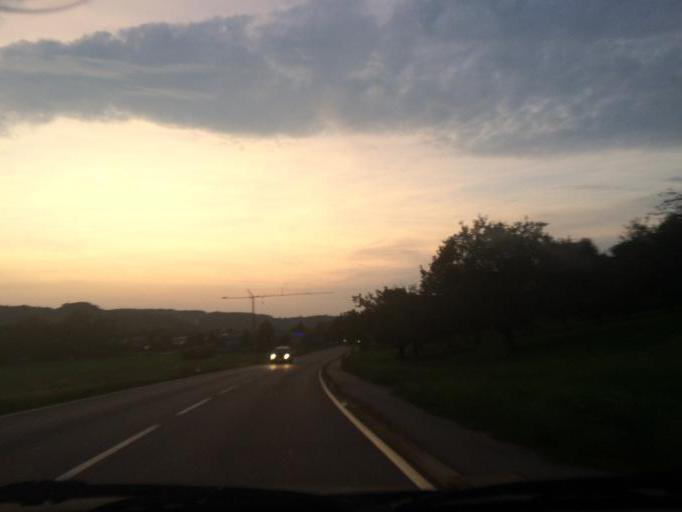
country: DE
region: Baden-Wuerttemberg
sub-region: Regierungsbezirk Stuttgart
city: Schorndorf
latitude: 48.8242
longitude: 9.5220
